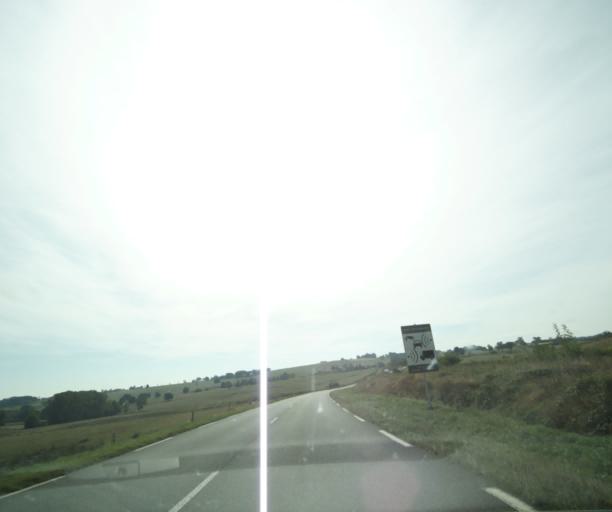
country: FR
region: Auvergne
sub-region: Departement de l'Allier
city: Le Donjon
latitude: 46.3201
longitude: 3.7687
